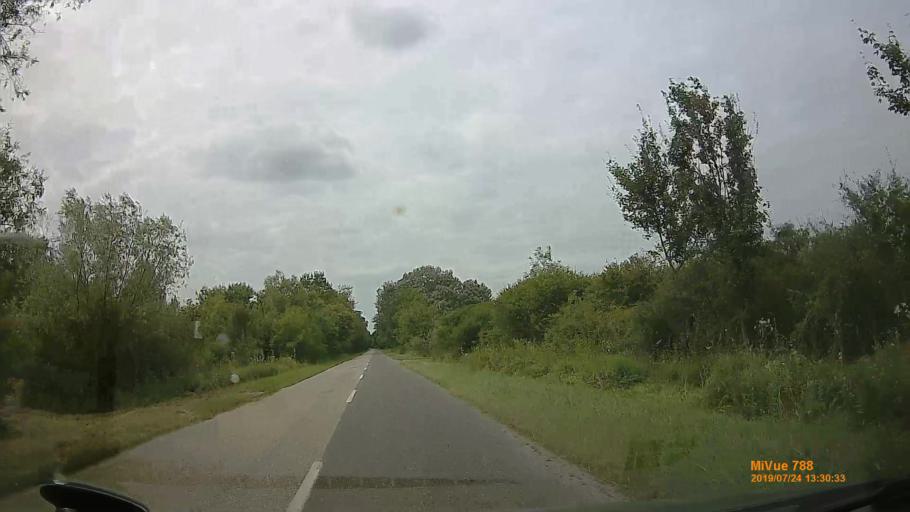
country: HU
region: Szabolcs-Szatmar-Bereg
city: Aranyosapati
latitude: 48.2310
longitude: 22.3770
